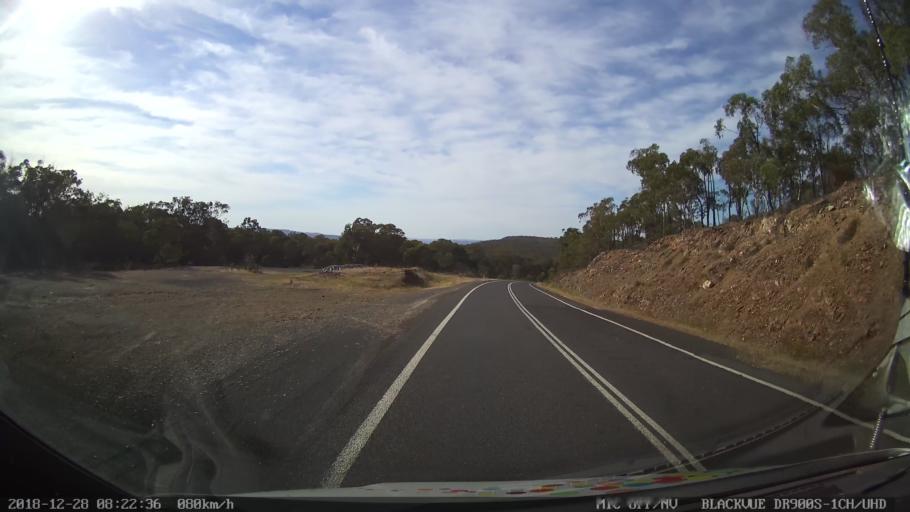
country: AU
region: New South Wales
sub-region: Blayney
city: Blayney
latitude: -33.8953
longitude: 149.3486
